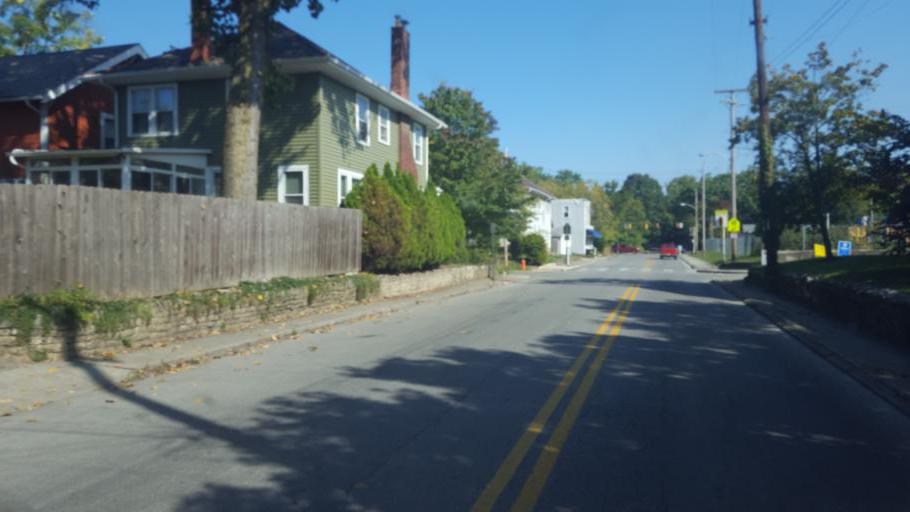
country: US
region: Ohio
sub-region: Franklin County
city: Grandview Heights
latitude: 40.0235
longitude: -83.0076
